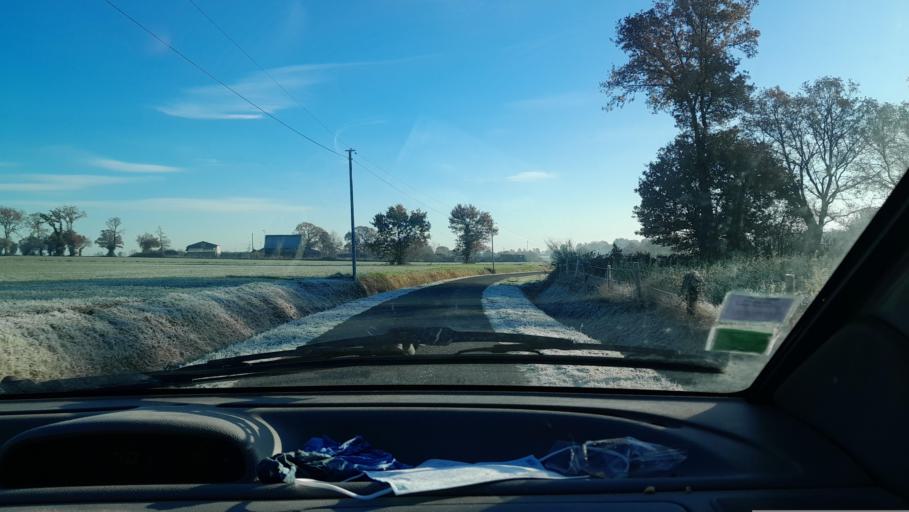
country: FR
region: Brittany
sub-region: Departement d'Ille-et-Vilaine
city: Rannee
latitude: 47.8690
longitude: -1.1869
